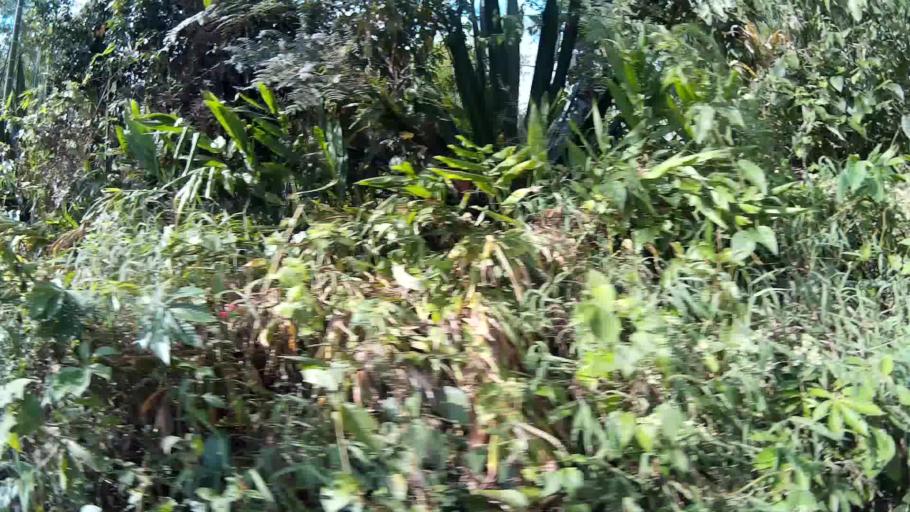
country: CO
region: Quindio
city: Filandia
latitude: 4.6919
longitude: -75.6732
